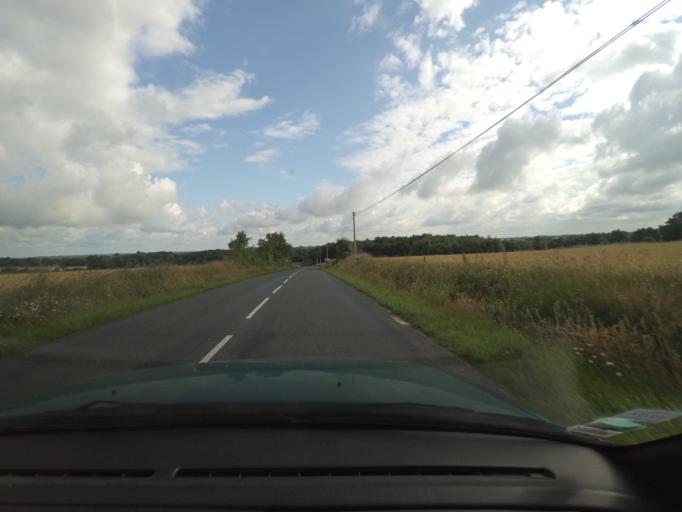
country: FR
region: Pays de la Loire
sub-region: Departement de la Vendee
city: Saint-Hilaire-de-Loulay
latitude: 47.0277
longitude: -1.3299
